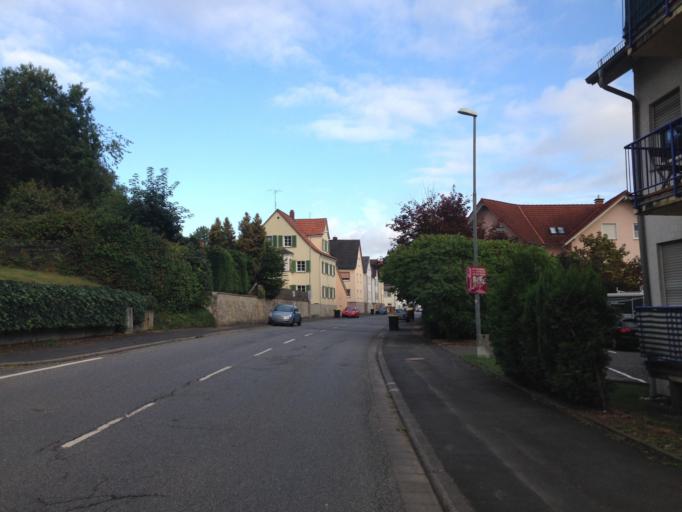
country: DE
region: Hesse
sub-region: Regierungsbezirk Giessen
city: Heuchelheim
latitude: 50.6239
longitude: 8.5848
